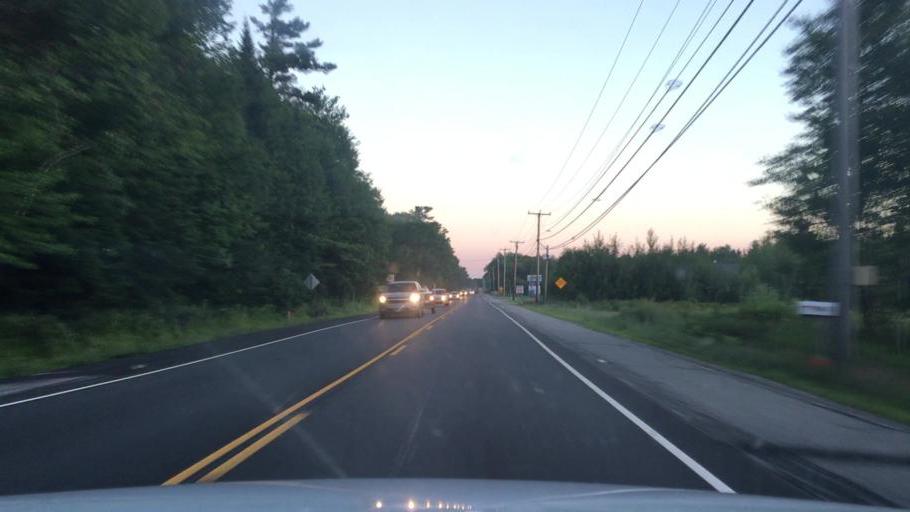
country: US
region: Maine
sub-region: Androscoggin County
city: Turner
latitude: 44.2152
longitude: -70.2461
